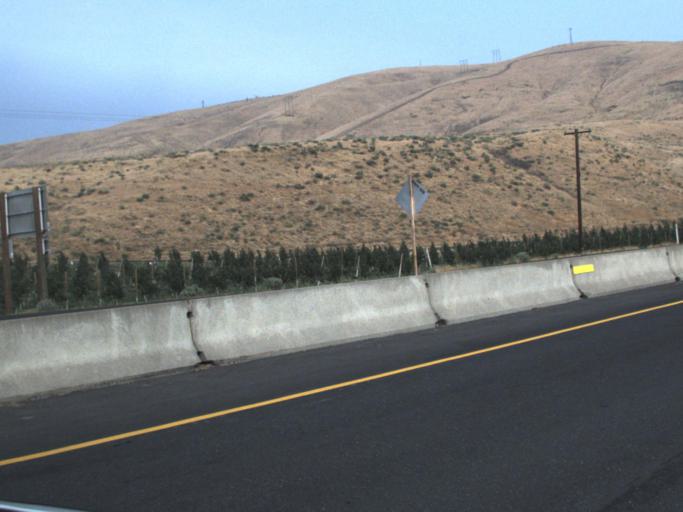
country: US
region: Washington
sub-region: Yakima County
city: Union Gap
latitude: 46.5201
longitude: -120.4806
